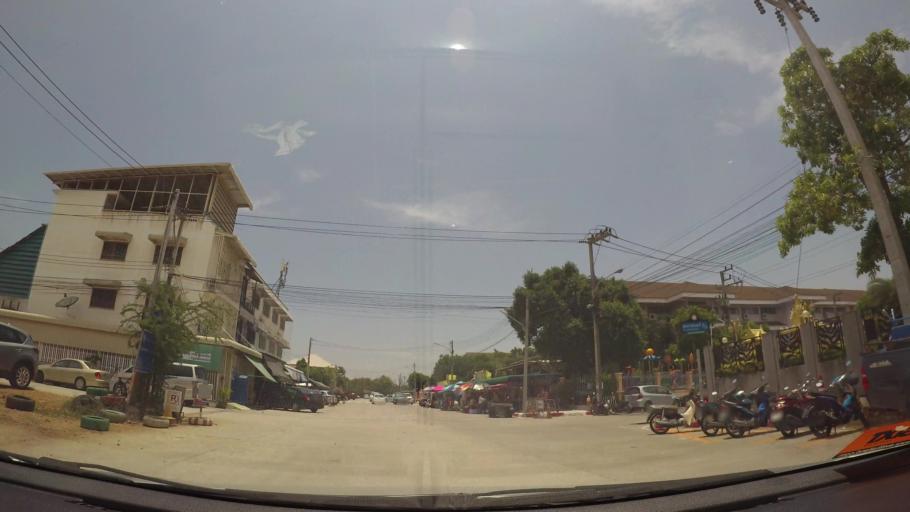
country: TH
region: Chon Buri
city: Chon Buri
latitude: 13.3400
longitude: 100.9412
